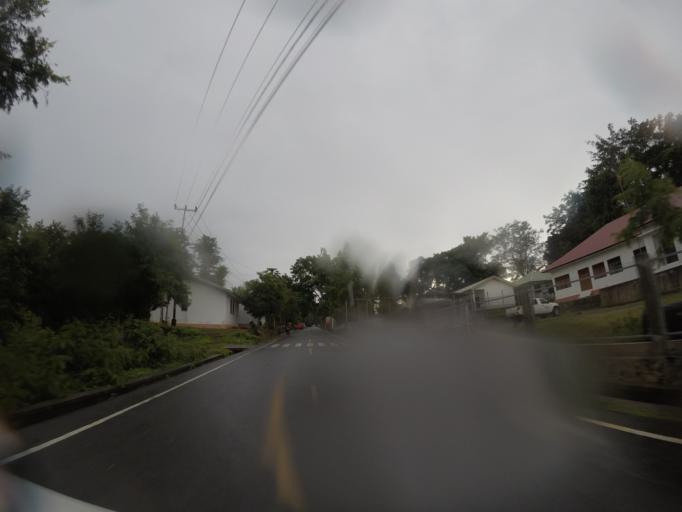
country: TL
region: Bobonaro
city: Maliana
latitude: -8.9688
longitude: 125.0408
